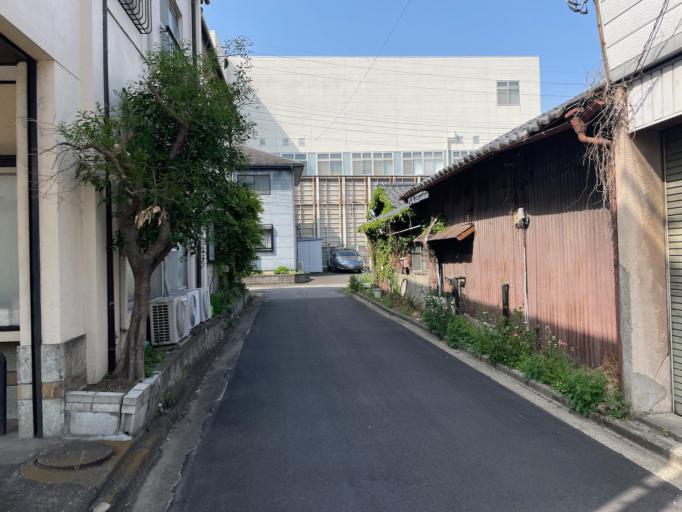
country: JP
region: Gunma
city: Ota
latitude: 36.2954
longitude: 139.3830
